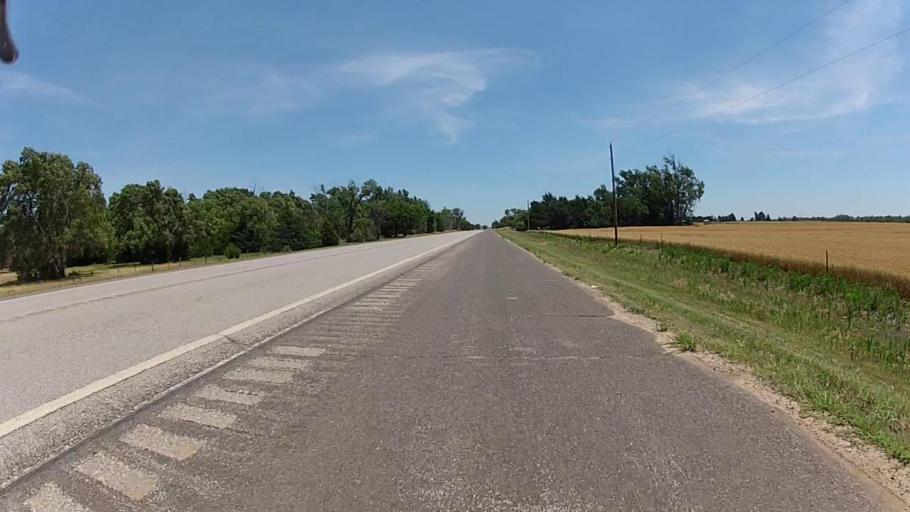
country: US
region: Kansas
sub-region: Barber County
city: Medicine Lodge
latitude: 37.2536
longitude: -98.4095
